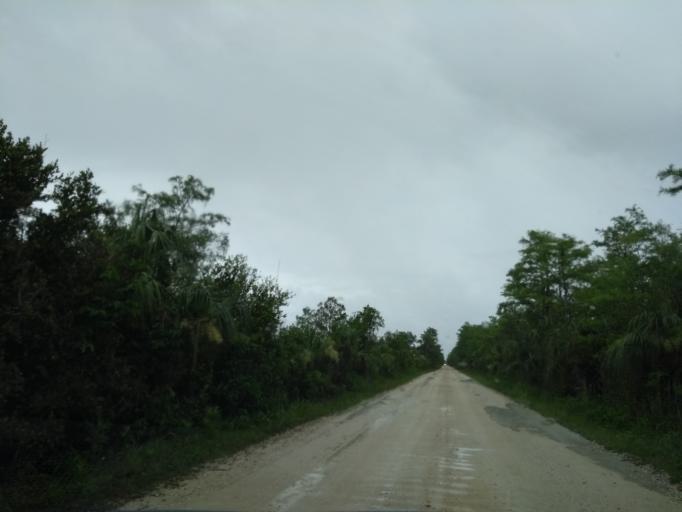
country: US
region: Florida
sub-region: Miami-Dade County
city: The Hammocks
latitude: 25.7602
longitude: -81.0228
